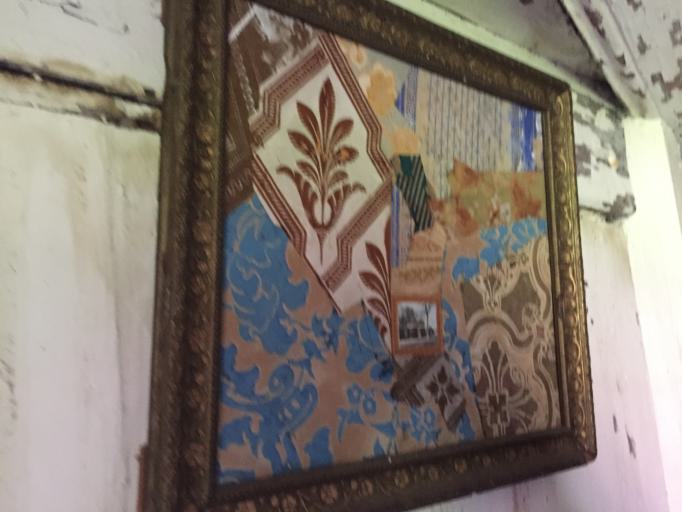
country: SE
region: Stockholm
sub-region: Norrtalje Kommun
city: Norrtalje
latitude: 59.5710
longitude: 18.5482
